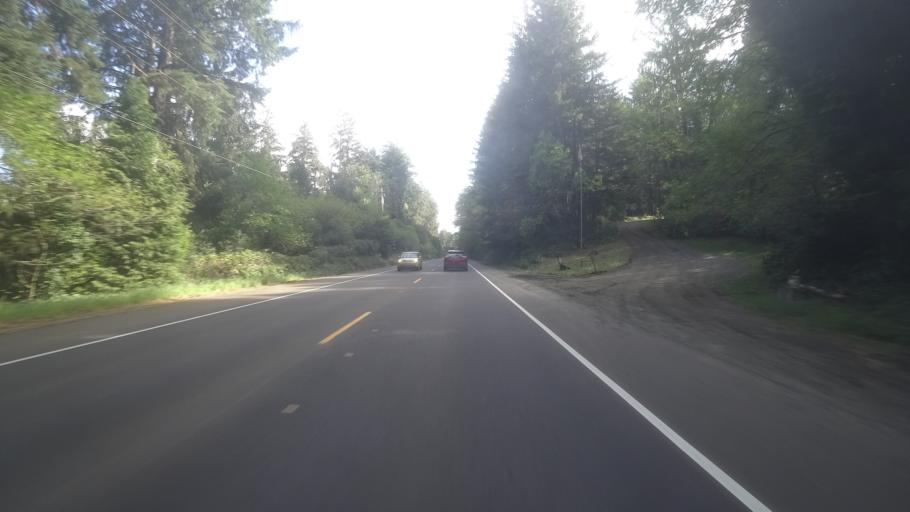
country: US
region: Oregon
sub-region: Lane County
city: Dunes City
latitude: 43.9124
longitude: -124.1113
